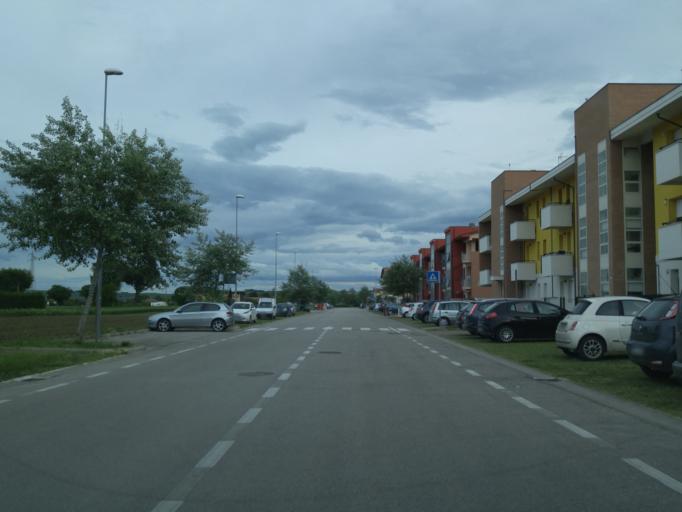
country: IT
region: The Marches
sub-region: Provincia di Pesaro e Urbino
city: Rosciano
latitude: 43.8052
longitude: 12.9935
